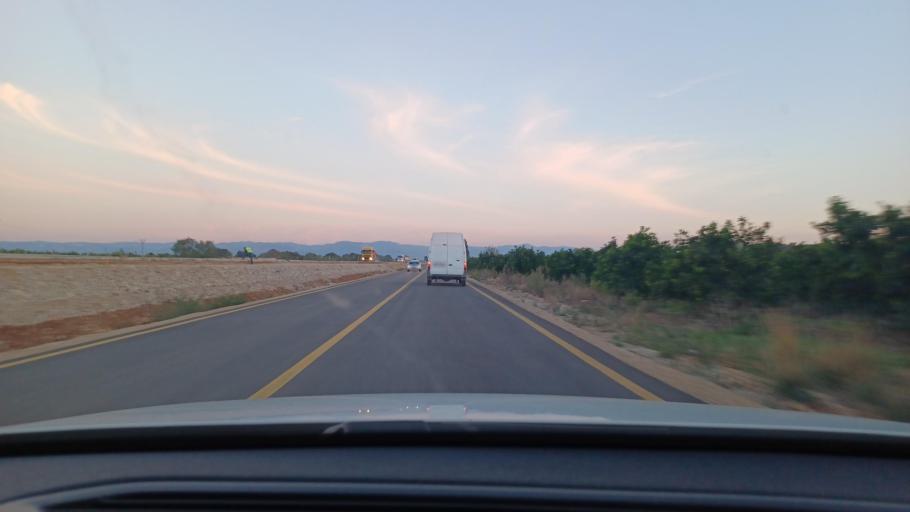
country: ES
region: Catalonia
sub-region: Provincia de Tarragona
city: Alcanar
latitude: 40.5320
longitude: 0.4437
